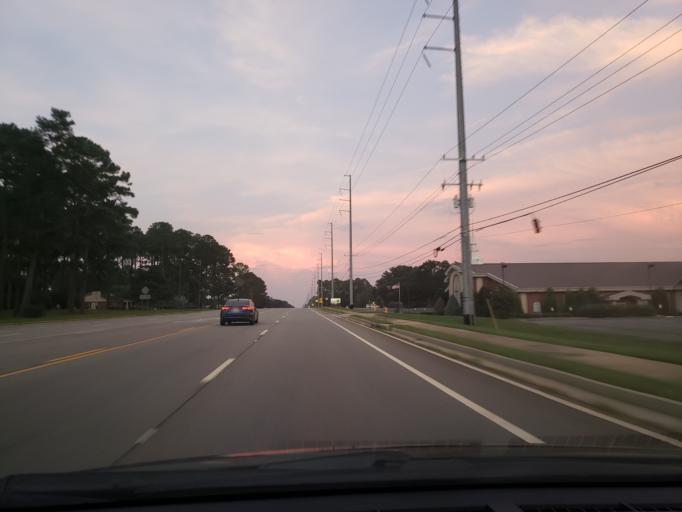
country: US
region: Georgia
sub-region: Dougherty County
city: Albany
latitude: 31.5856
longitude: -84.2808
